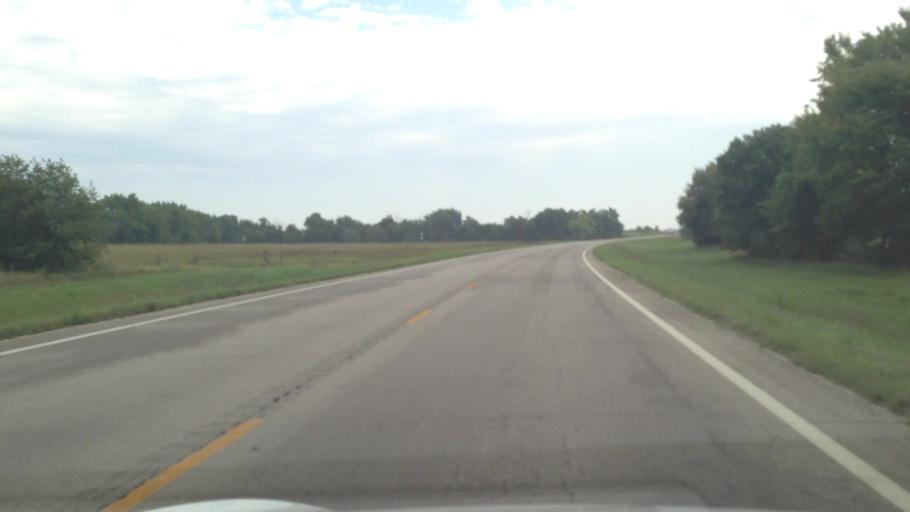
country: US
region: Kansas
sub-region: Bourbon County
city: Fort Scott
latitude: 37.8918
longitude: -95.0403
